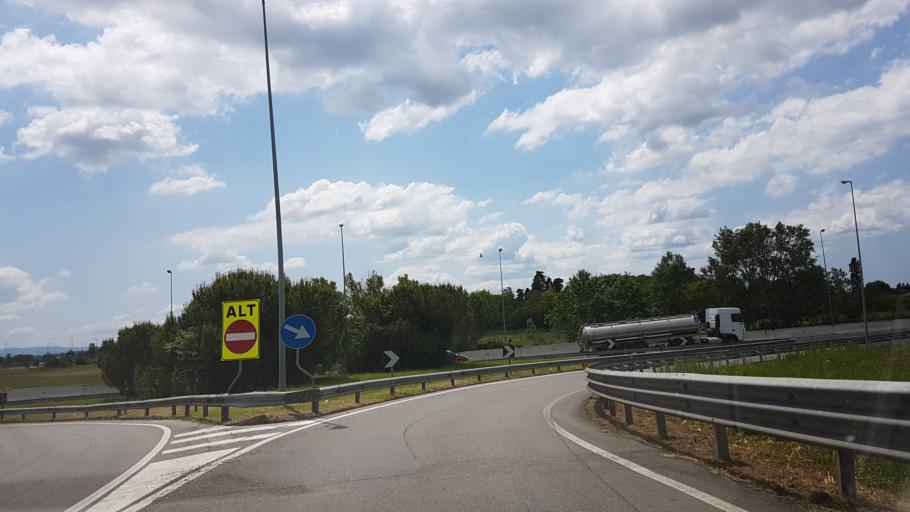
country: IT
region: Tuscany
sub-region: Provincia di Livorno
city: Vicarello
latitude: 43.6238
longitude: 10.4649
